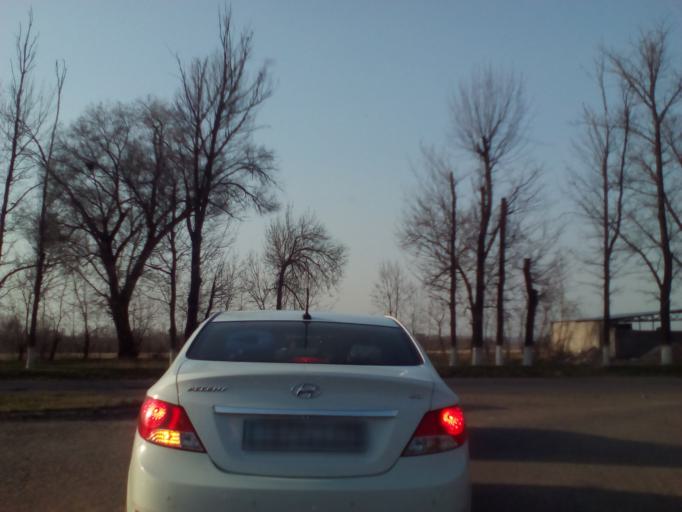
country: KZ
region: Almaty Oblysy
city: Burunday
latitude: 43.1825
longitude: 76.5140
